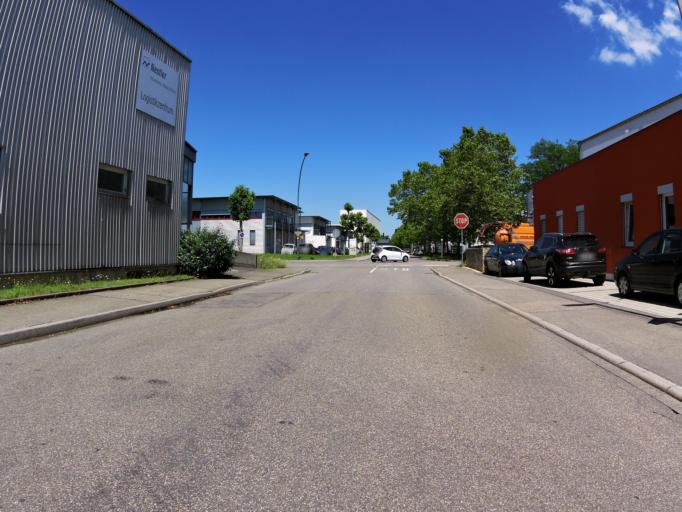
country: DE
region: Baden-Wuerttemberg
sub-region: Freiburg Region
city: Lahr
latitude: 48.3412
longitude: 7.8294
